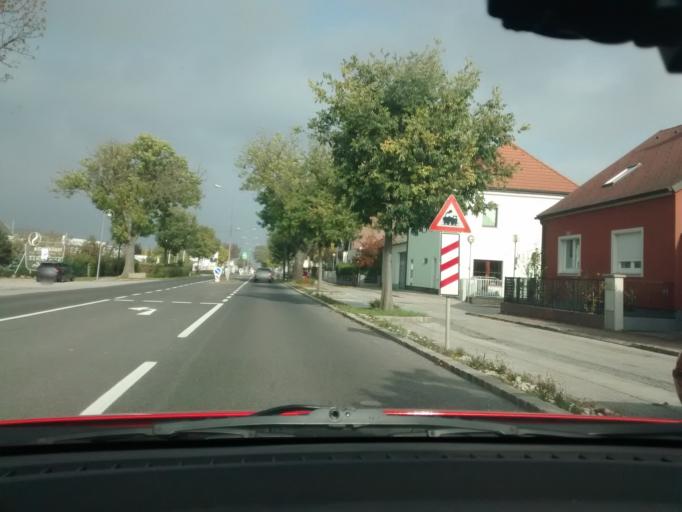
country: AT
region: Lower Austria
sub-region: Politischer Bezirk Baden
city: Traiskirchen
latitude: 48.0229
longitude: 16.2983
